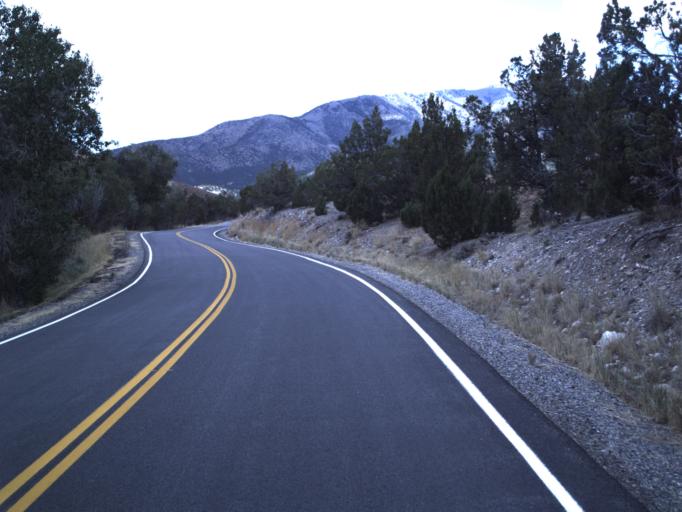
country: US
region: Utah
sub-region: Tooele County
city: Grantsville
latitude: 40.3356
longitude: -112.5284
